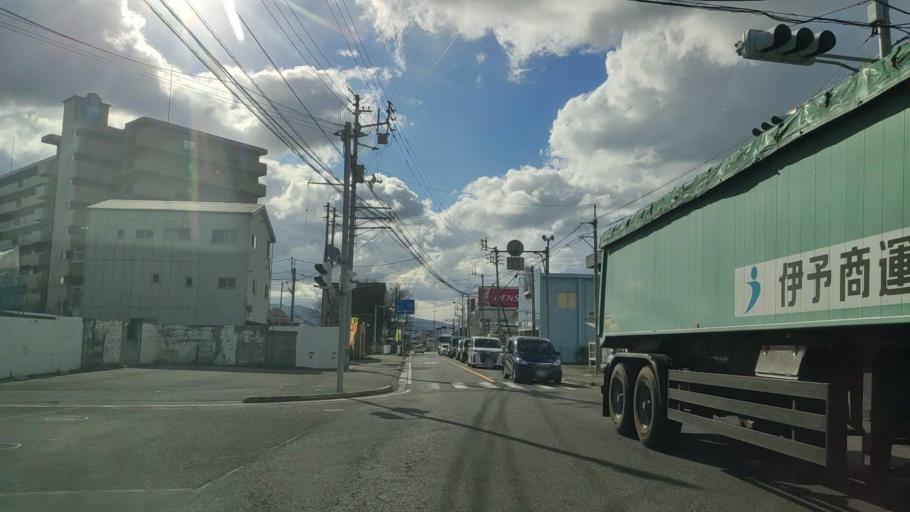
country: JP
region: Ehime
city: Masaki-cho
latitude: 33.8300
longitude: 132.7085
